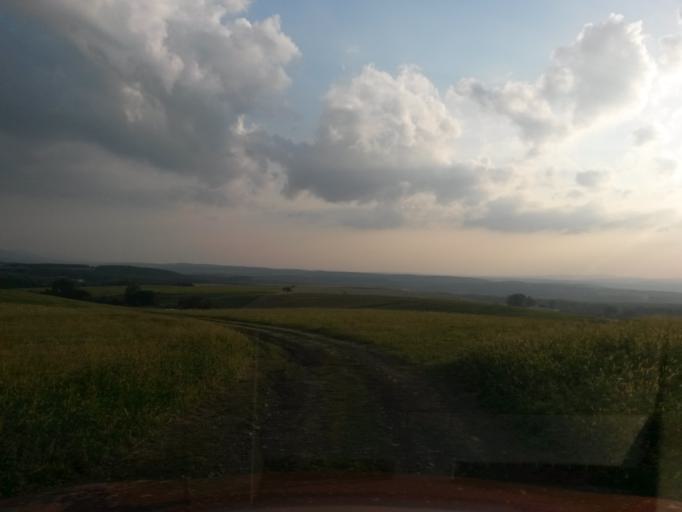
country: SK
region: Kosicky
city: Secovce
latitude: 48.8098
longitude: 21.4765
